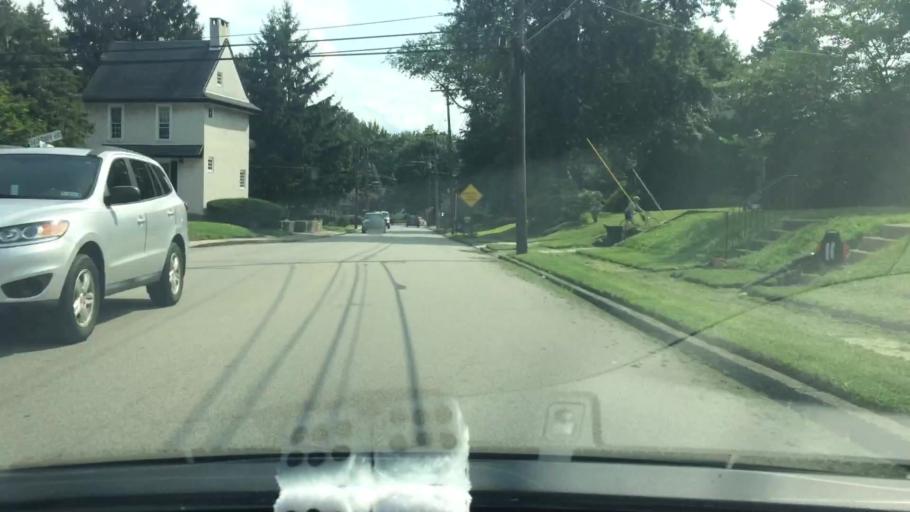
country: US
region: Pennsylvania
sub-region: Delaware County
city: Morton
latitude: 39.9121
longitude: -75.3245
